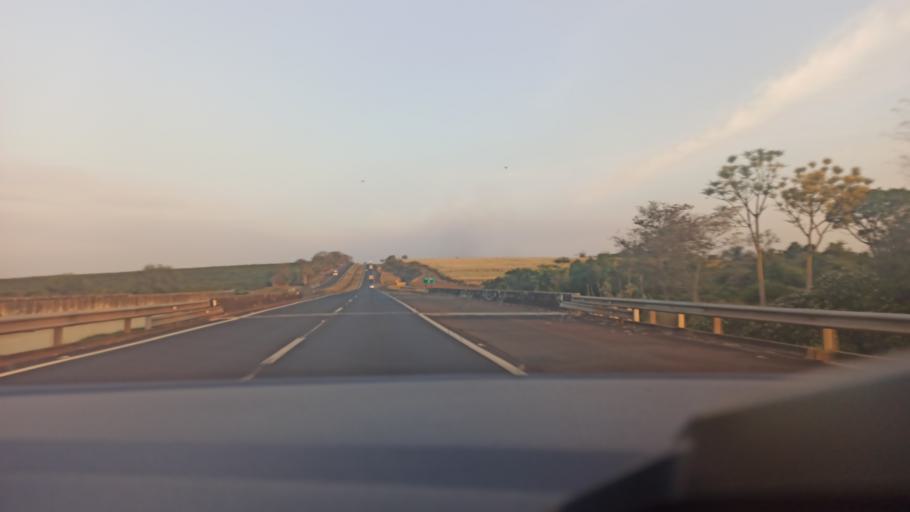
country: BR
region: Sao Paulo
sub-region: Taquaritinga
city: Taquaritinga
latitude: -21.4334
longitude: -48.6598
